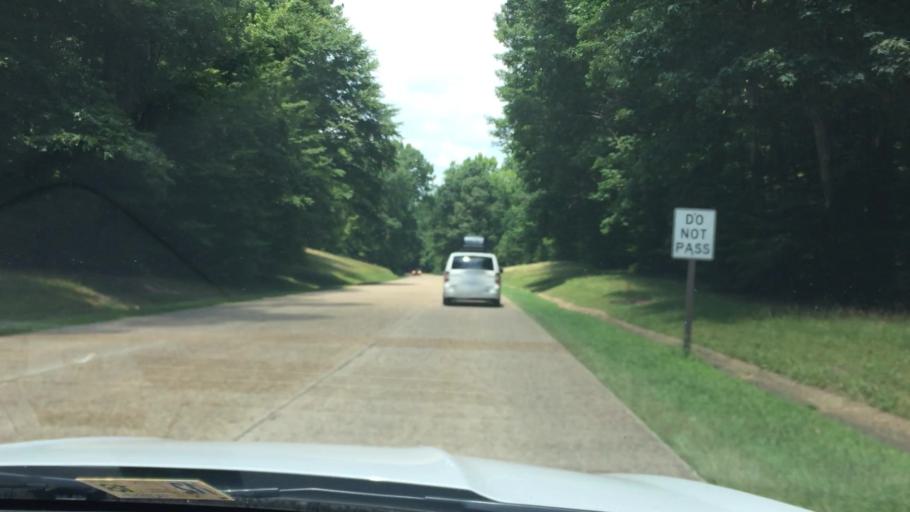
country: US
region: Virginia
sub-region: York County
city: Yorktown
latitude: 37.2359
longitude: -76.5220
